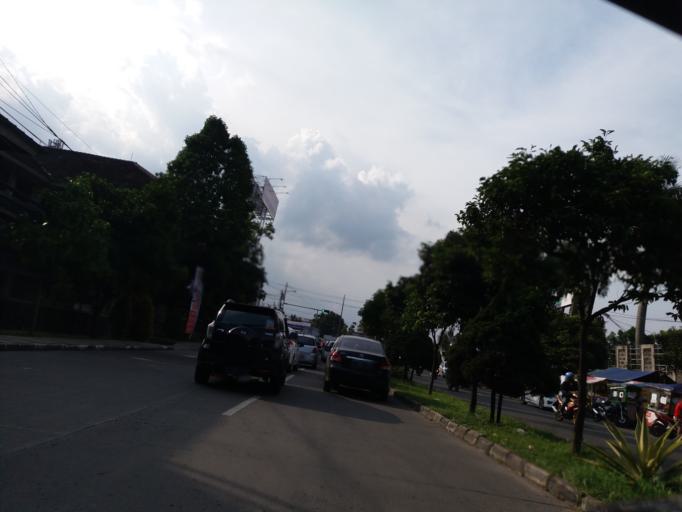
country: ID
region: West Java
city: Bandung
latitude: -6.9504
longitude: 107.6261
